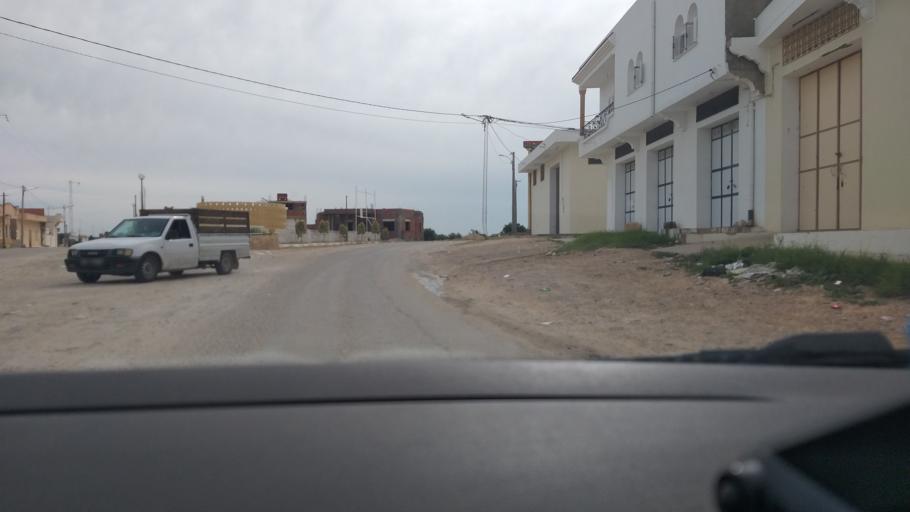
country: TN
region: Al Mahdiyah
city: El Jem
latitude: 35.2835
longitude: 10.7125
